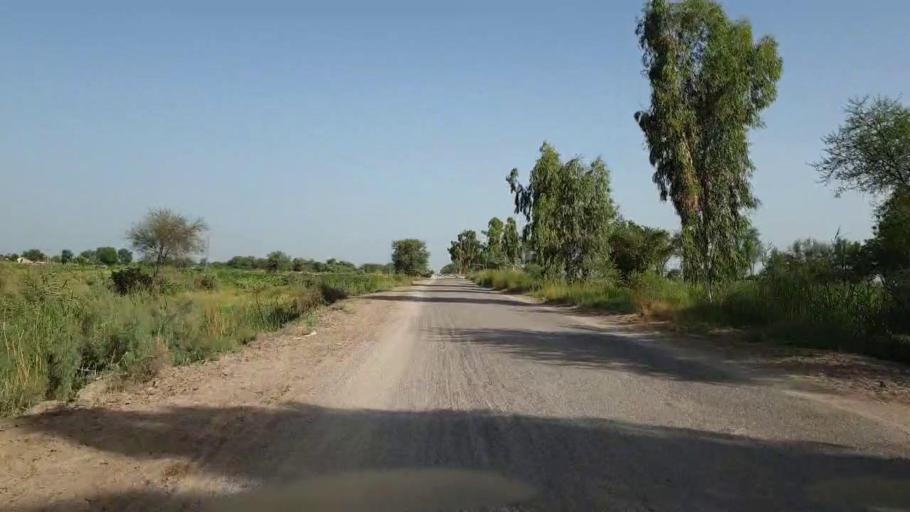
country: PK
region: Sindh
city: Nawabshah
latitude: 26.1631
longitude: 68.4430
